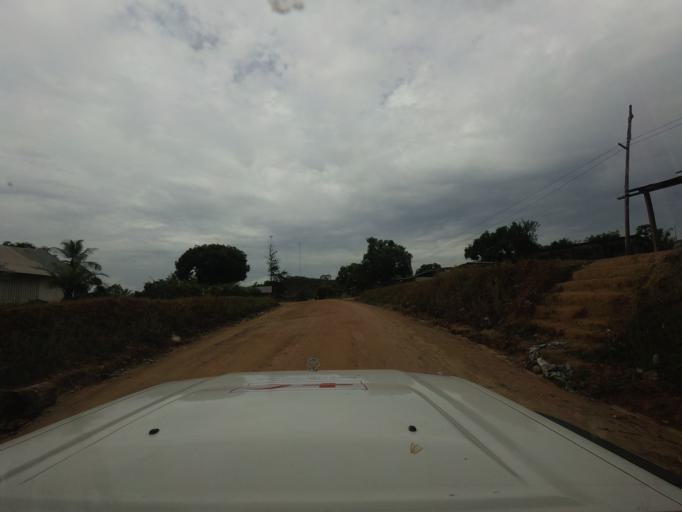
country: SL
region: Eastern Province
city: Buedu
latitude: 8.2829
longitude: -10.0901
